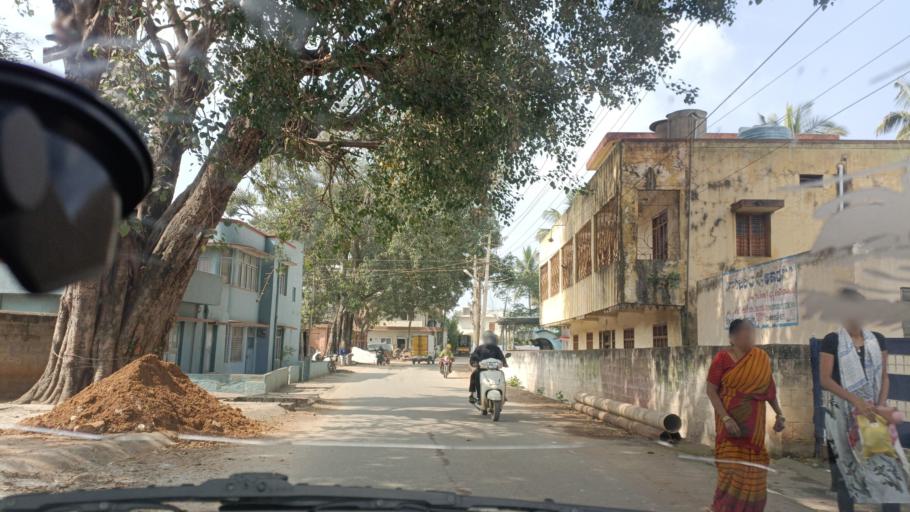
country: IN
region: Karnataka
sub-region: Bangalore Urban
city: Yelahanka
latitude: 13.1562
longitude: 77.6177
